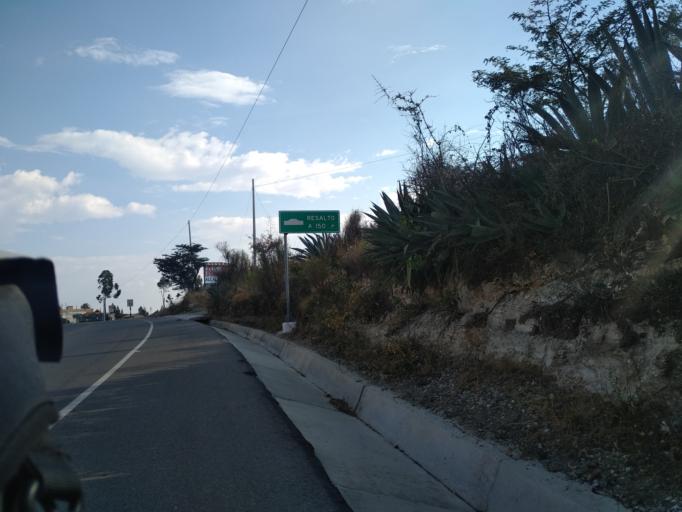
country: PE
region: Cajamarca
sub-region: San Marcos
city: San Marcos
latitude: -7.3814
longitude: -78.1254
